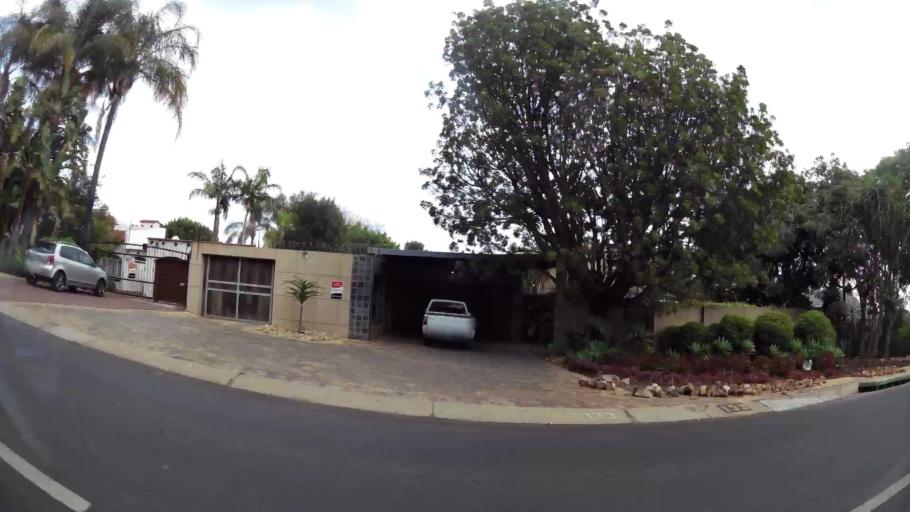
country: ZA
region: Gauteng
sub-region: City of Tshwane Metropolitan Municipality
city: Pretoria
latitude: -25.7631
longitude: 28.3111
